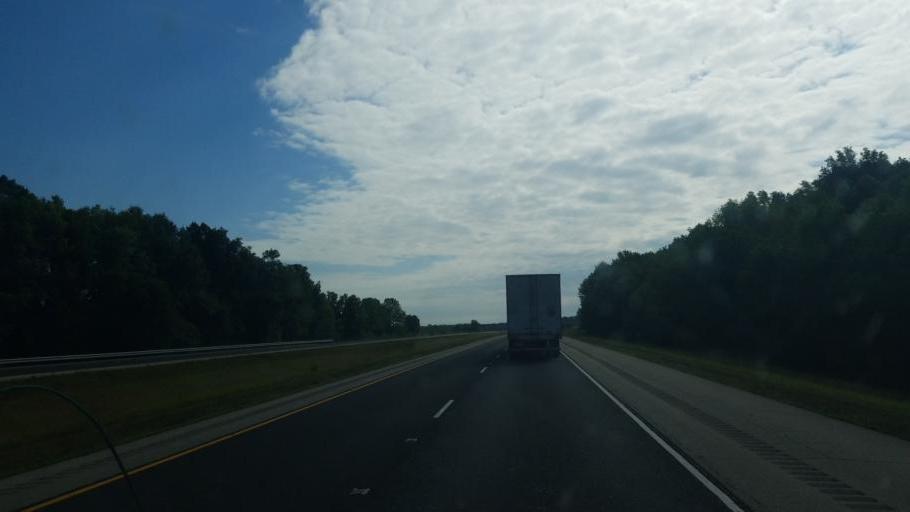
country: US
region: Illinois
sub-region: Clark County
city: Marshall
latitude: 39.3974
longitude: -87.7789
